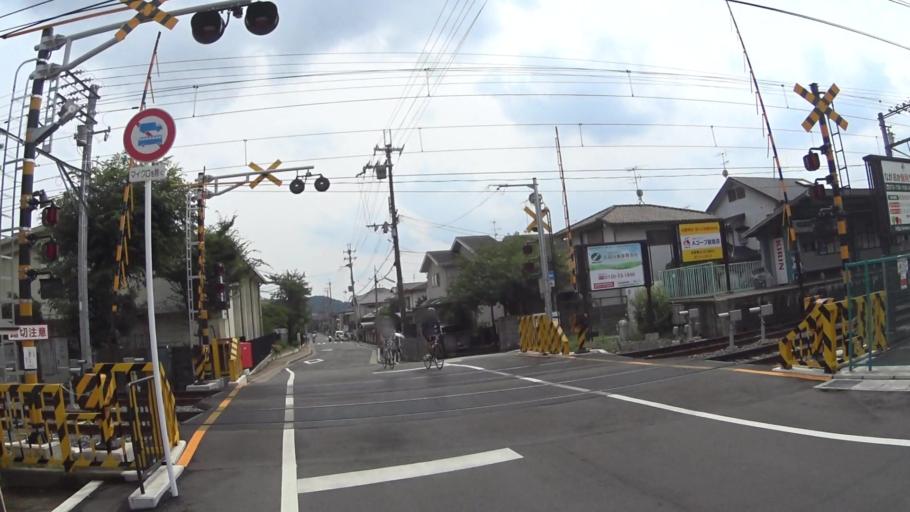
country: JP
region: Kyoto
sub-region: Kyoto-shi
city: Kamigyo-ku
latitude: 35.0712
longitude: 135.7869
